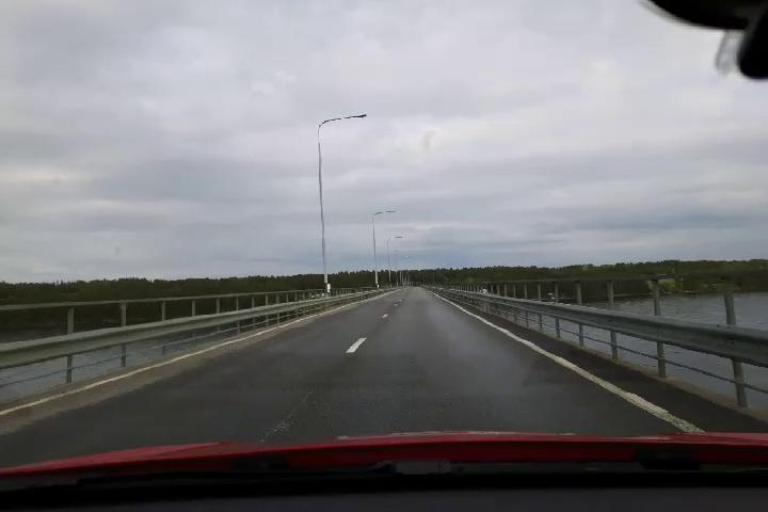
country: SE
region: Jaemtland
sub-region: Bergs Kommun
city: Hoverberg
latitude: 62.9774
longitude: 14.4687
